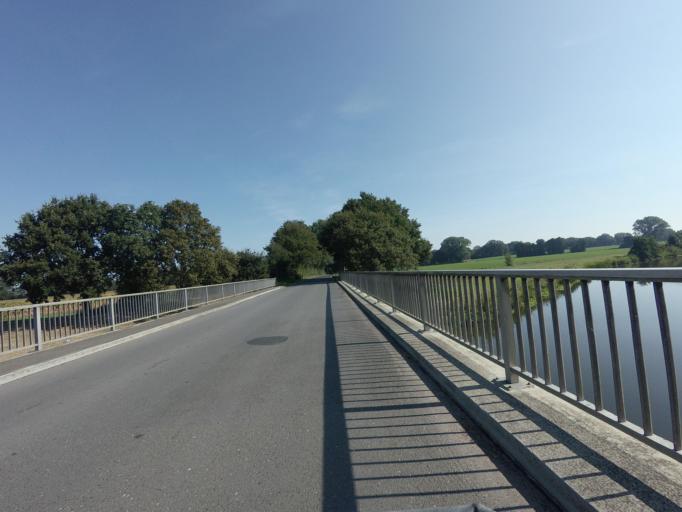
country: DE
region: Lower Saxony
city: Emlichheim
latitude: 52.6030
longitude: 6.7973
